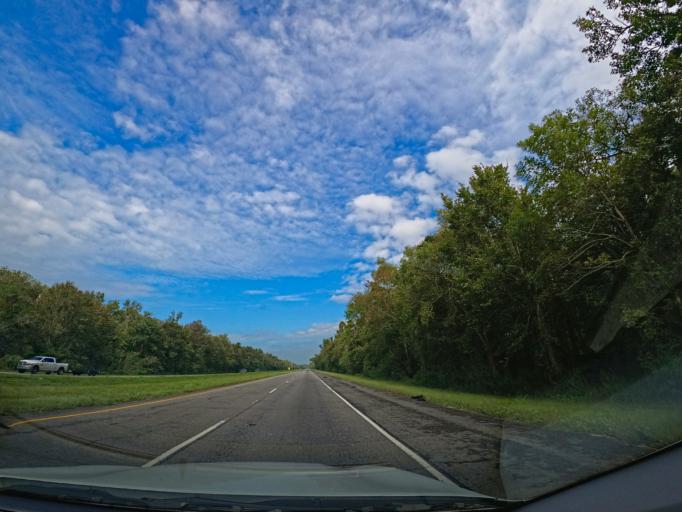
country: US
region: Louisiana
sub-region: Saint Mary Parish
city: Patterson
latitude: 29.7103
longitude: -91.3939
